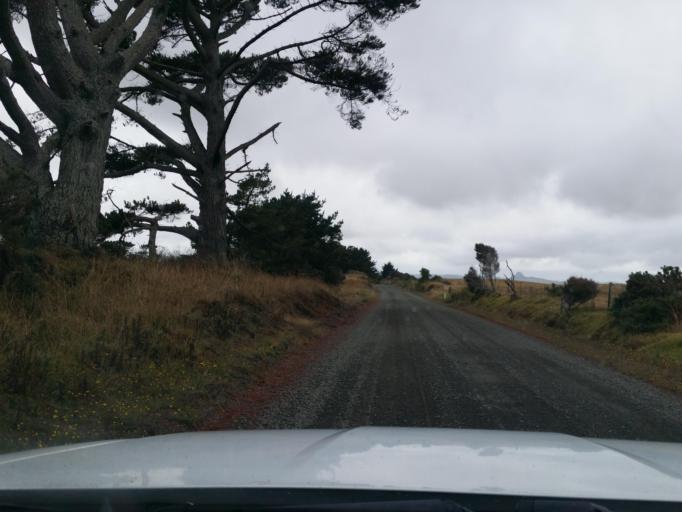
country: NZ
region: Northland
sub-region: Kaipara District
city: Dargaville
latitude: -36.0365
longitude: 173.8565
